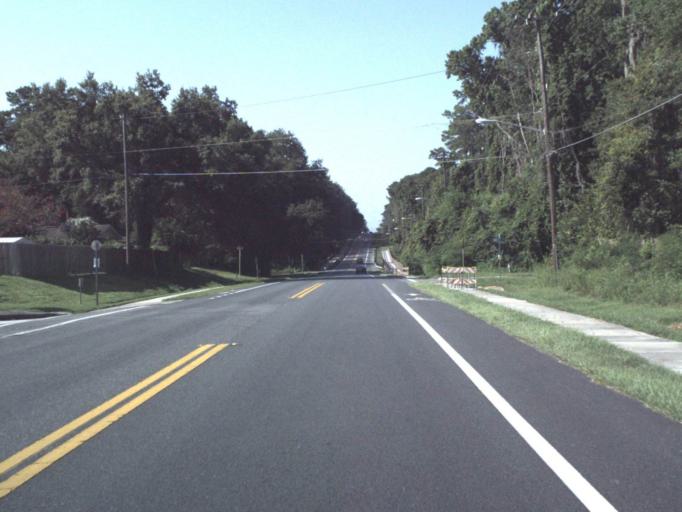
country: US
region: Florida
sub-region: Alachua County
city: Gainesville
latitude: 29.6766
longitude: -82.3724
